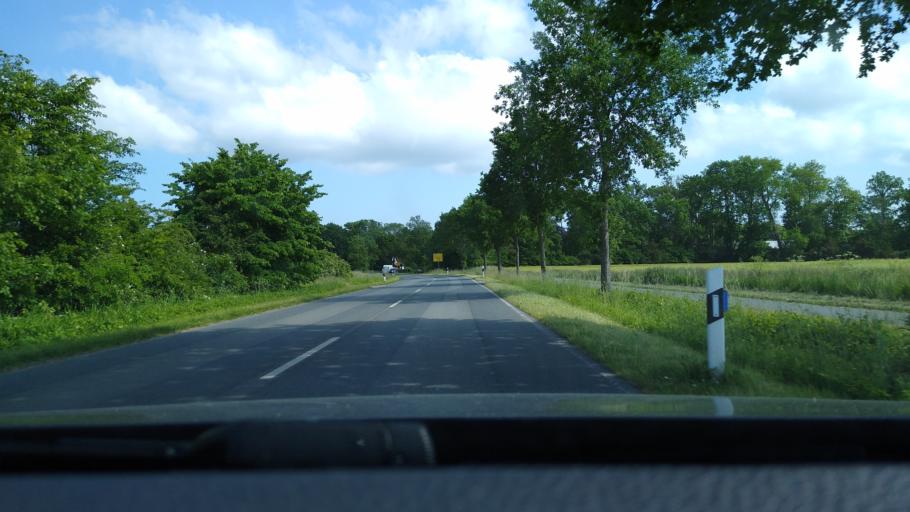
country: DE
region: Schleswig-Holstein
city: Riepsdorf
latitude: 54.1941
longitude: 10.9817
